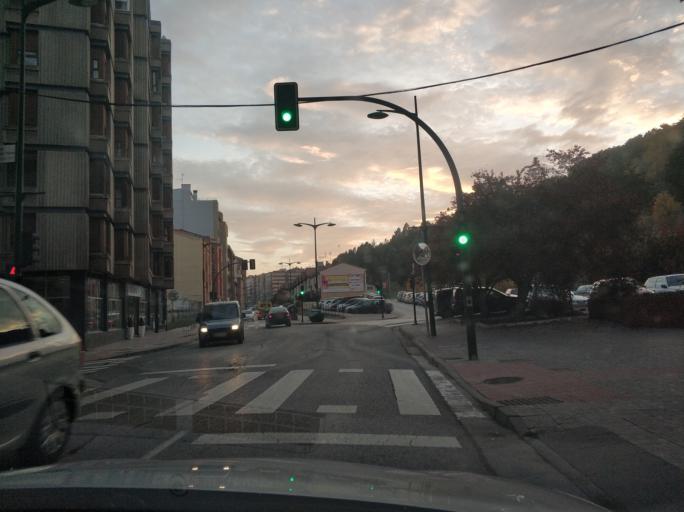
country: ES
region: Castille and Leon
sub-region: Provincia de Burgos
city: Burgos
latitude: 42.3494
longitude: -3.6988
